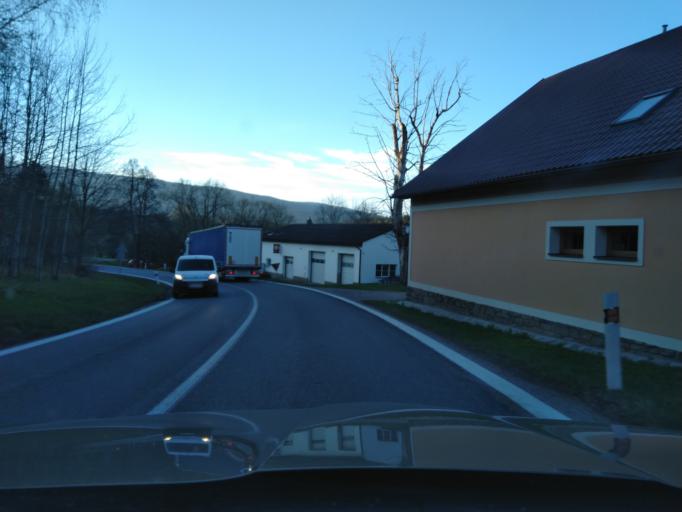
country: CZ
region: Jihocesky
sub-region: Okres Prachatice
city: Vimperk
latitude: 49.0302
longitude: 13.7631
